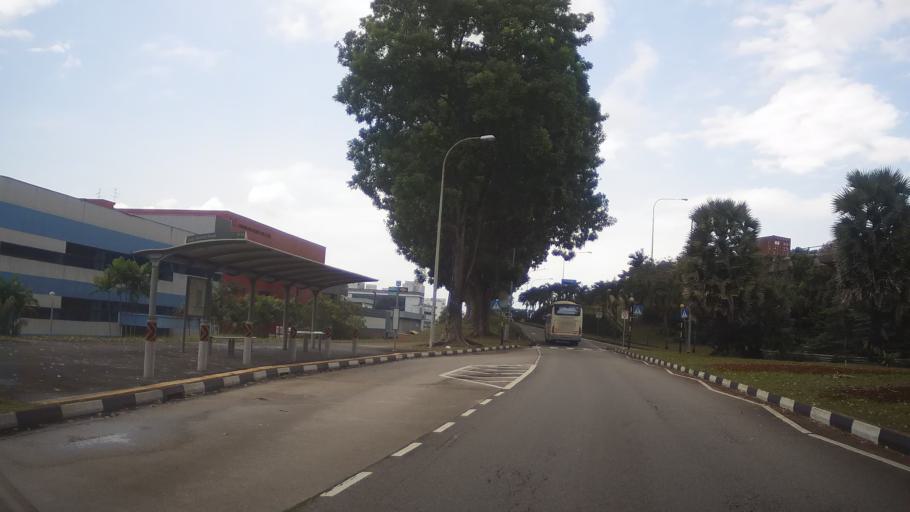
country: MY
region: Johor
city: Johor Bahru
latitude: 1.3304
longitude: 103.6753
